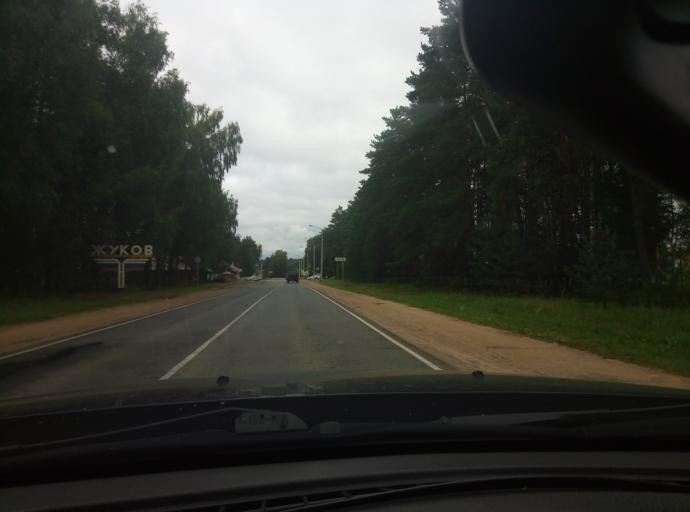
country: RU
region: Kaluga
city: Zhukovo
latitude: 55.0155
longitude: 36.7512
